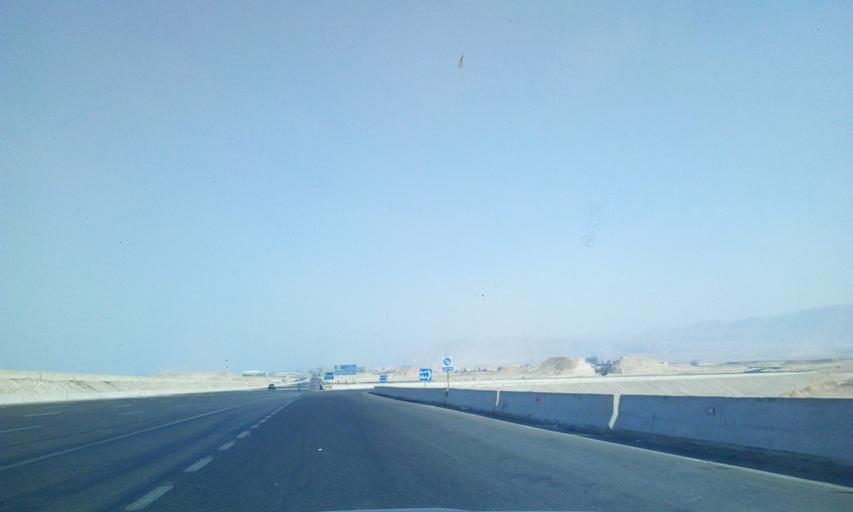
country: EG
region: As Suways
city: Ain Sukhna
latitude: 29.6734
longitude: 32.2317
